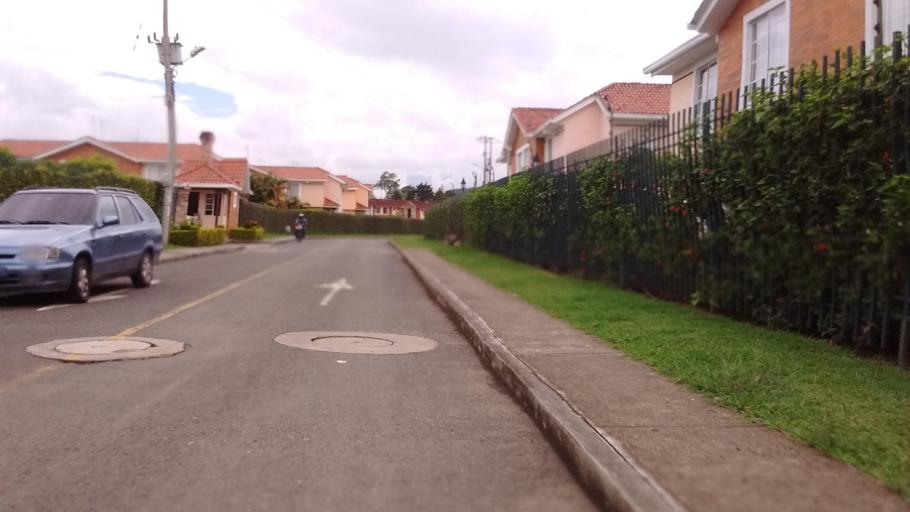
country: CO
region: Cauca
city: Popayan
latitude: 2.4783
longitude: -76.5814
